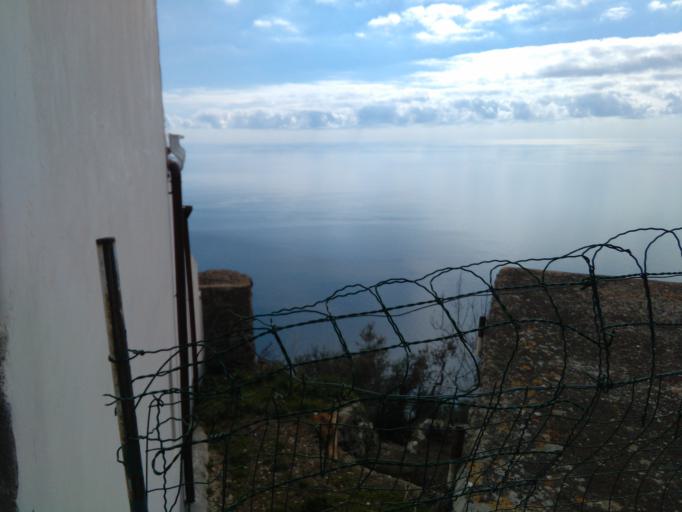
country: IT
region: Campania
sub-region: Provincia di Salerno
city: Positano
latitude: 40.6290
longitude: 14.5046
